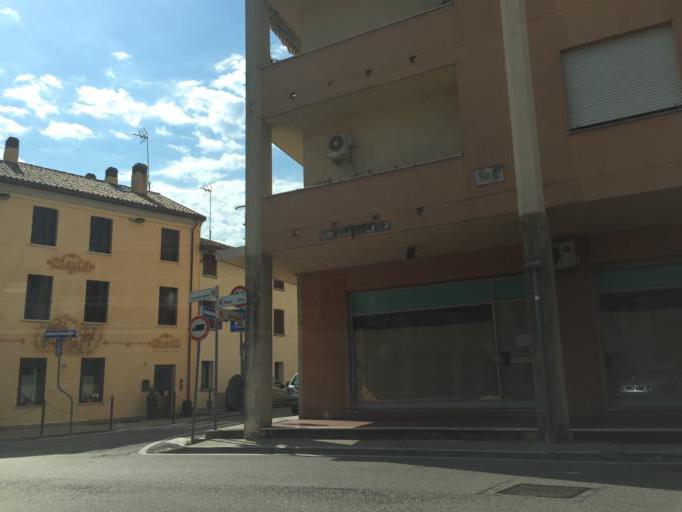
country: IT
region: Friuli Venezia Giulia
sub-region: Provincia di Pordenone
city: Sacile
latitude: 45.9540
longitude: 12.4965
